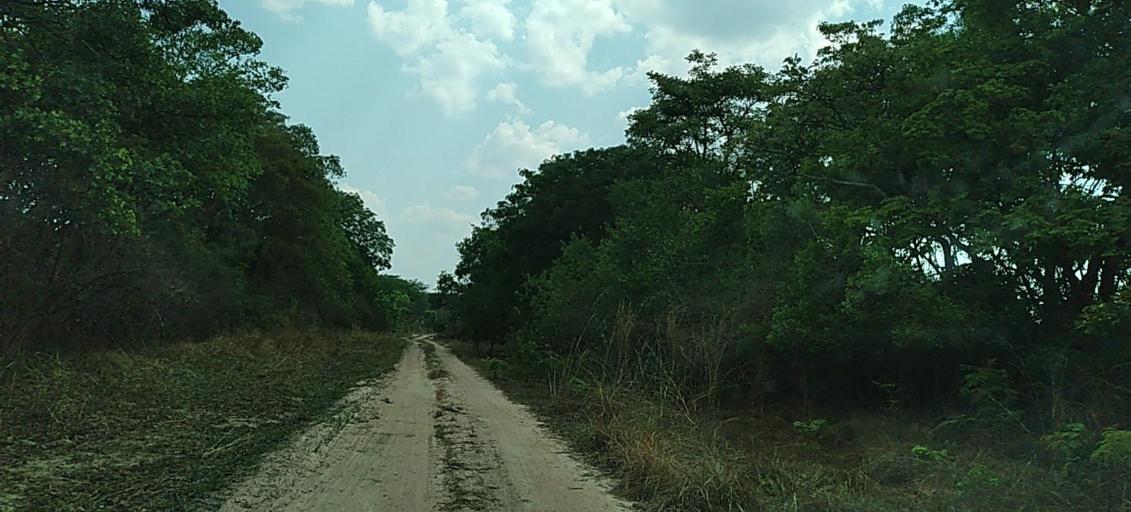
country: ZM
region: Copperbelt
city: Mpongwe
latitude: -13.8586
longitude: 27.9282
